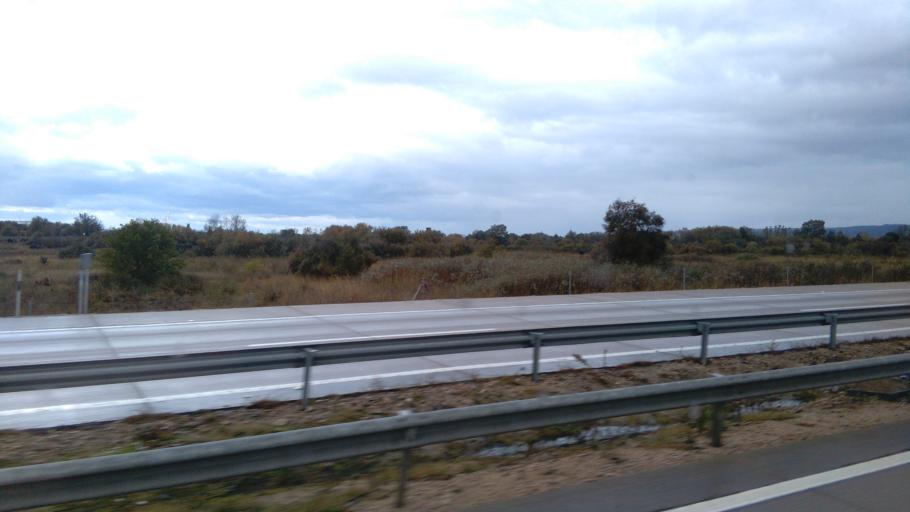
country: ES
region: Castille-La Mancha
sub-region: Province of Toledo
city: Talavera de la Reina
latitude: 39.9835
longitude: -4.7533
